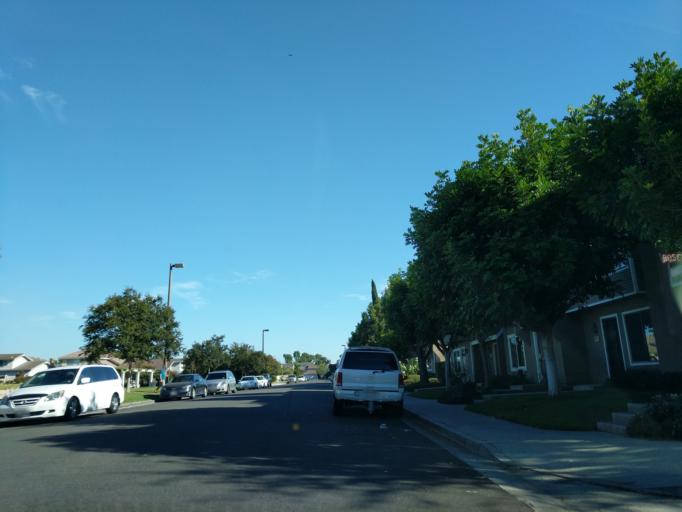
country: US
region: California
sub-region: Orange County
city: Irvine
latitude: 33.6832
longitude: -117.8039
